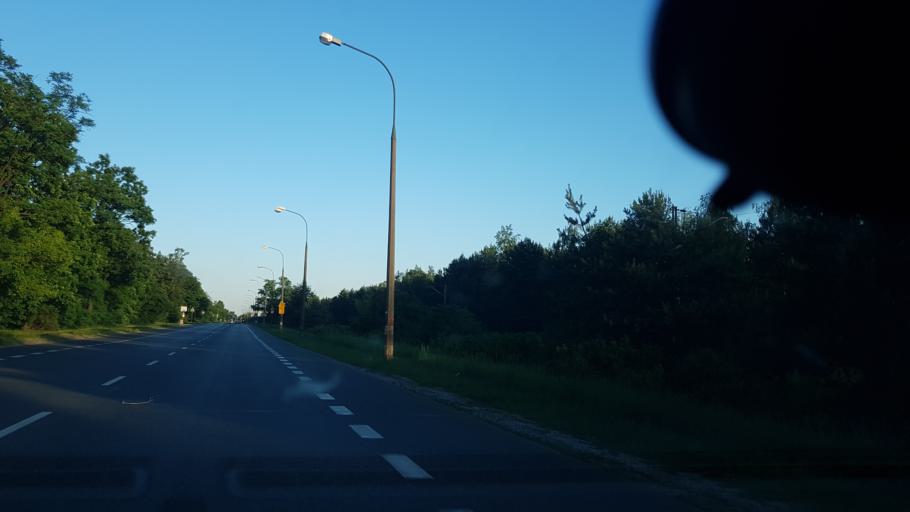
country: PL
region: Masovian Voivodeship
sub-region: Warszawa
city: Wawer
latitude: 52.1997
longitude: 21.1738
